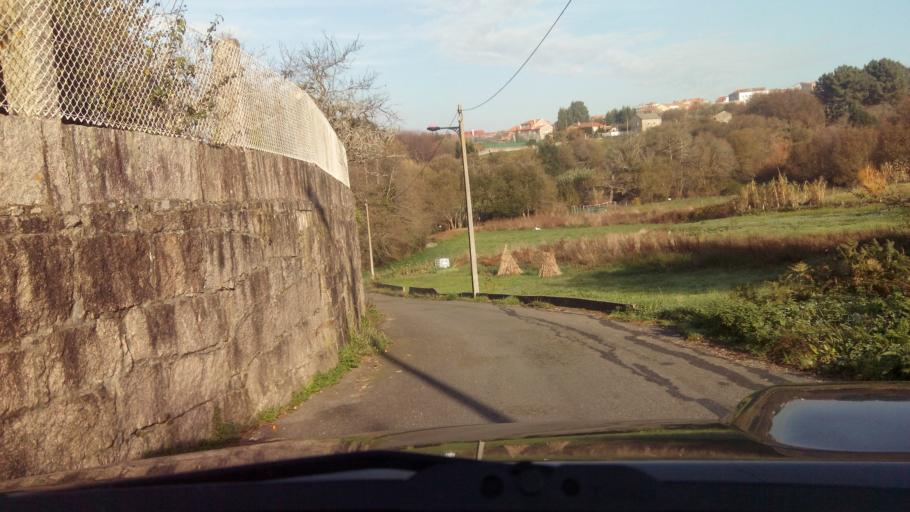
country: ES
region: Galicia
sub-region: Provincia de Pontevedra
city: Marin
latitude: 42.3629
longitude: -8.7324
